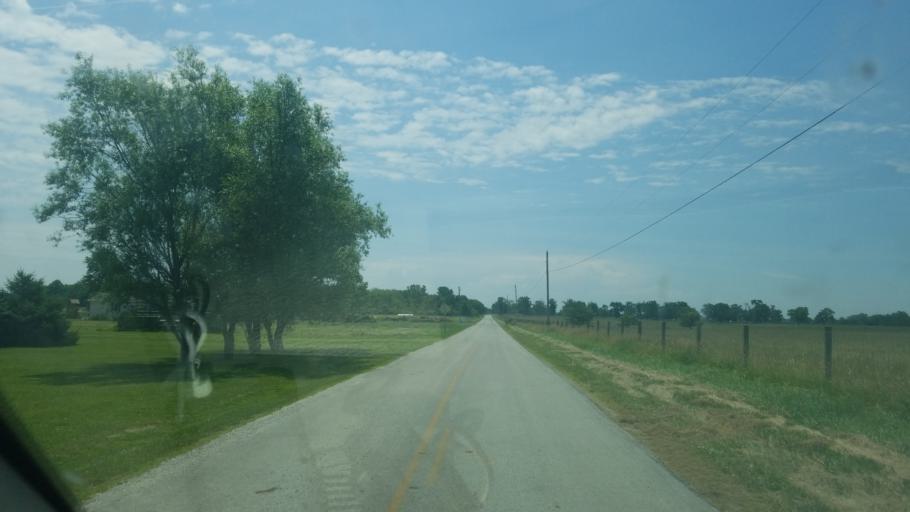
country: US
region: Ohio
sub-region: Wood County
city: North Baltimore
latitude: 41.2398
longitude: -83.6212
